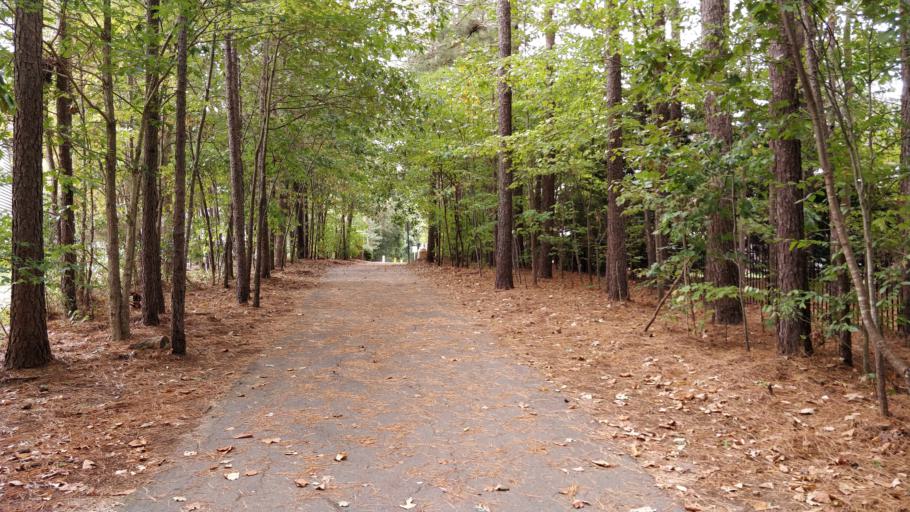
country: US
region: North Carolina
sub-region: Wake County
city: West Raleigh
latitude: 35.9041
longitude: -78.6696
